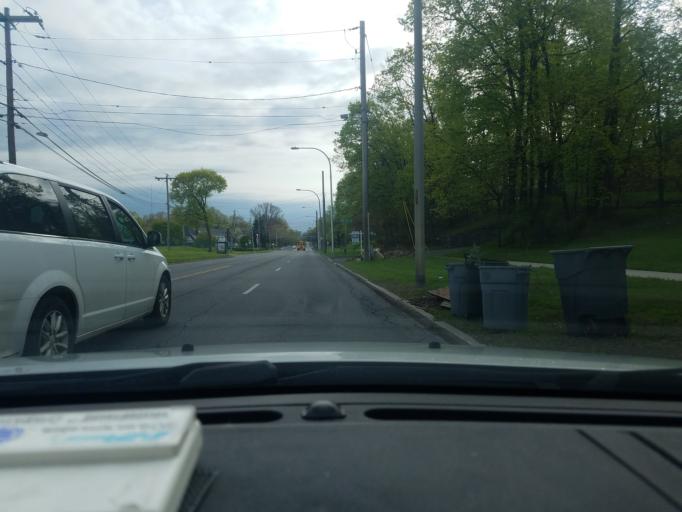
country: US
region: New York
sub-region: Onondaga County
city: Lyncourt
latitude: 43.0638
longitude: -76.1253
